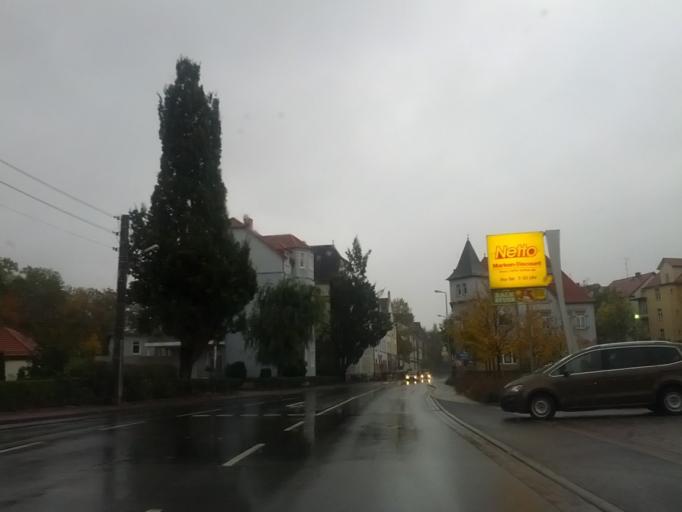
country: DE
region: Thuringia
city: Gotha
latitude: 50.9489
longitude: 10.7139
